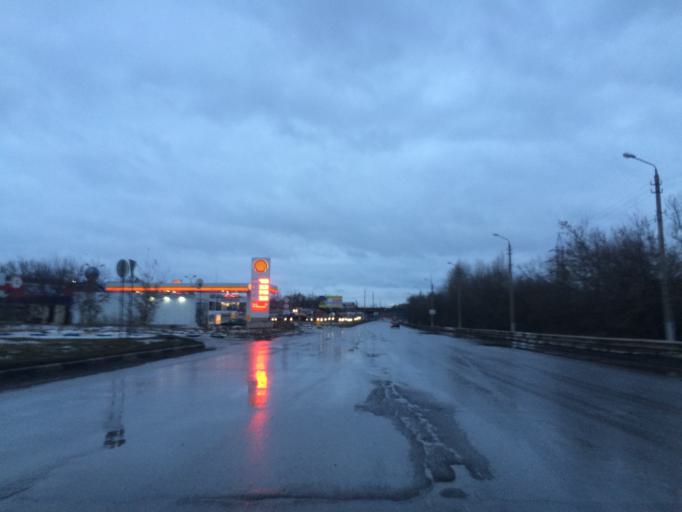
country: RU
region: Tula
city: Tula
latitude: 54.1742
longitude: 37.6405
